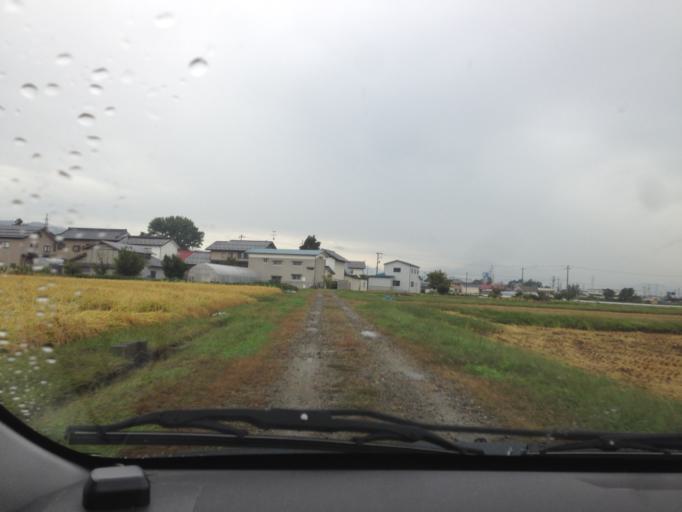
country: JP
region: Fukushima
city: Kitakata
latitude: 37.5200
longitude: 139.9057
